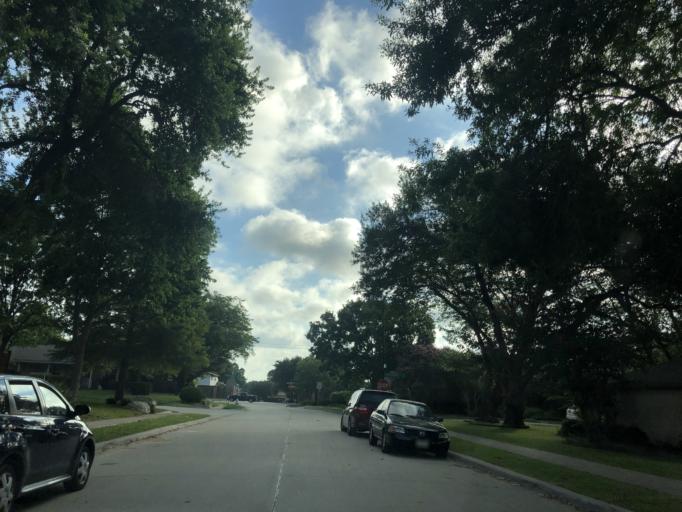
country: US
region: Texas
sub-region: Dallas County
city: Garland
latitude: 32.8583
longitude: -96.6408
